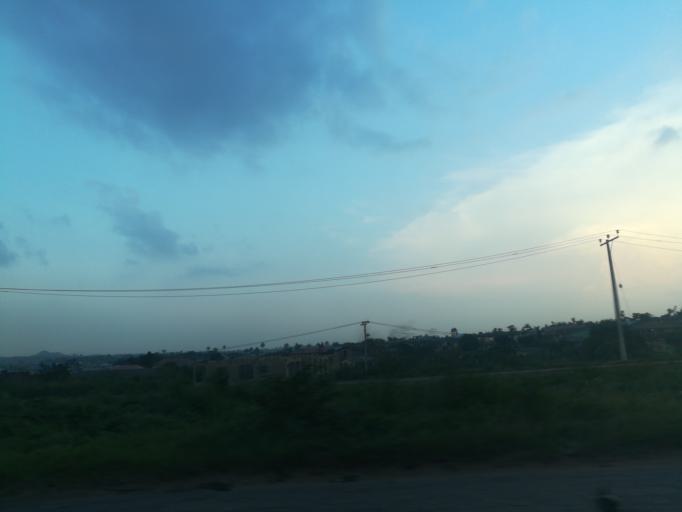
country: NG
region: Oyo
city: Ibadan
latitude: 7.4385
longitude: 3.9276
